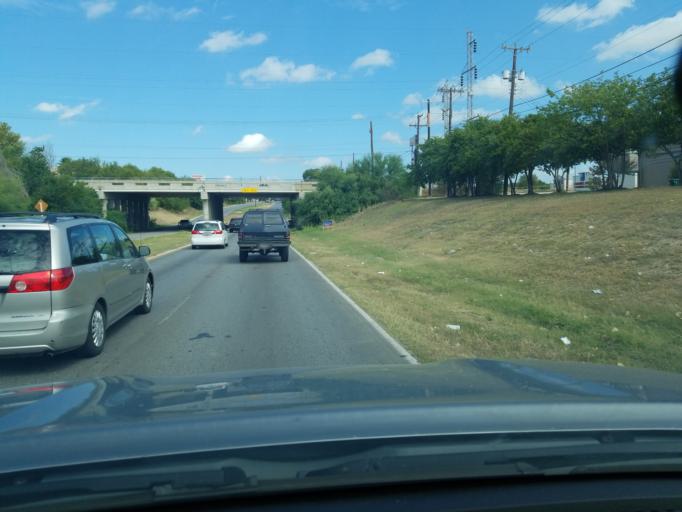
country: US
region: Texas
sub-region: Bexar County
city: Terrell Hills
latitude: 29.4931
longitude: -98.4330
